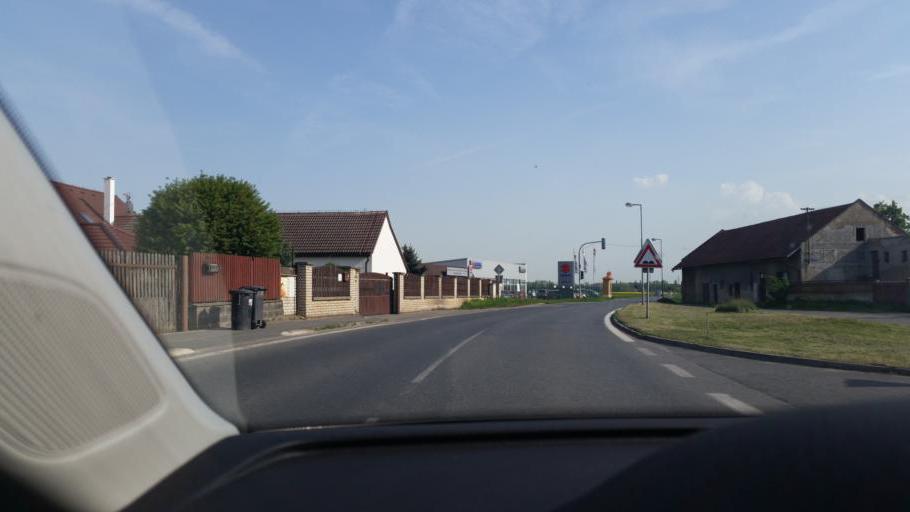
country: CZ
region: Central Bohemia
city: Veltruby
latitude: 50.0720
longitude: 15.1917
